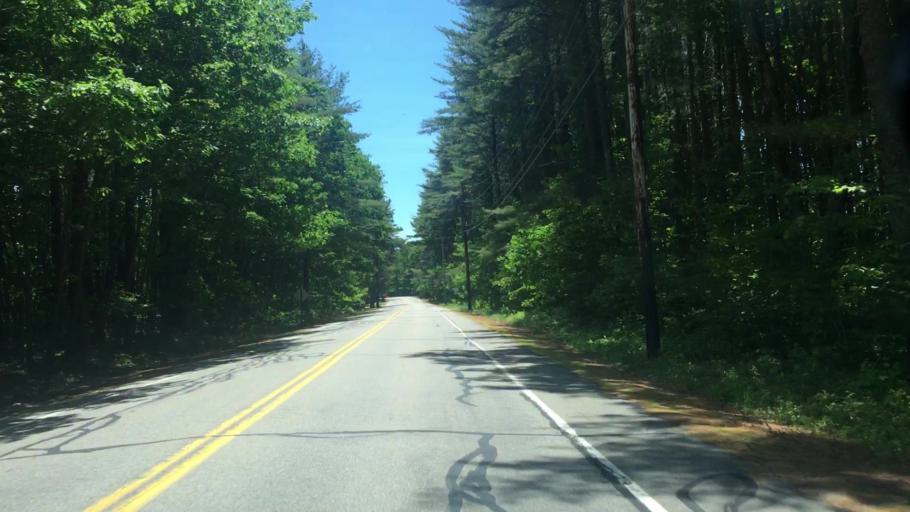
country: US
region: Maine
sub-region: York County
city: Kennebunk
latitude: 43.3719
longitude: -70.5270
